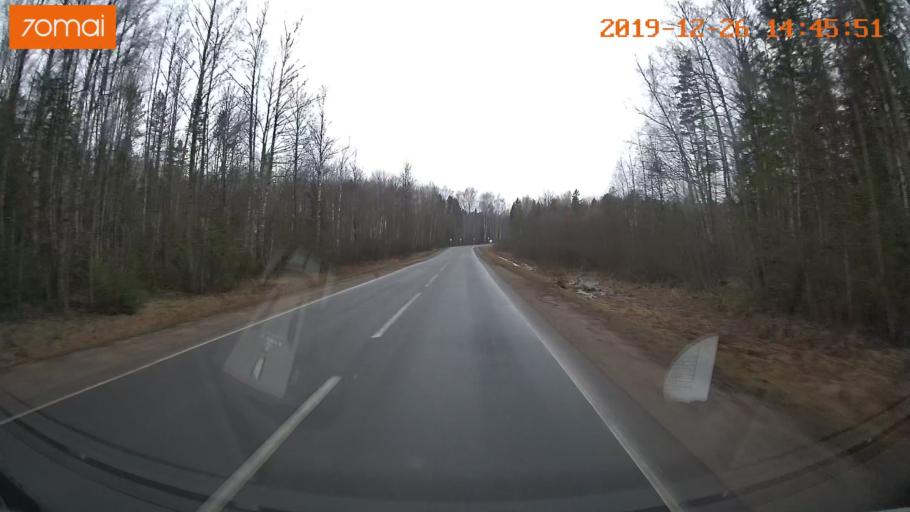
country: RU
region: Jaroslavl
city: Poshekhon'ye
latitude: 58.3355
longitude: 39.0301
